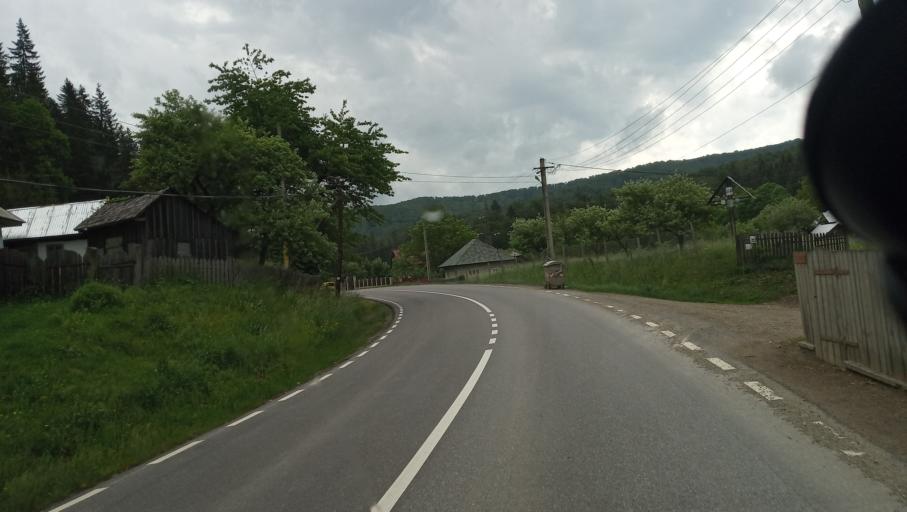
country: RO
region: Neamt
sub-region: Comuna Pipirig
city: Dolhesti
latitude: 47.1963
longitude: 26.0495
